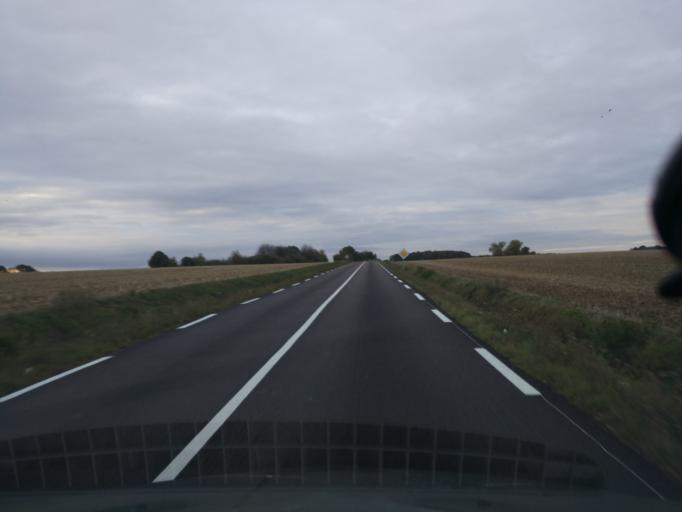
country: FR
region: Ile-de-France
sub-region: Departement de l'Essonne
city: Les Molieres
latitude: 48.6687
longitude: 2.0656
